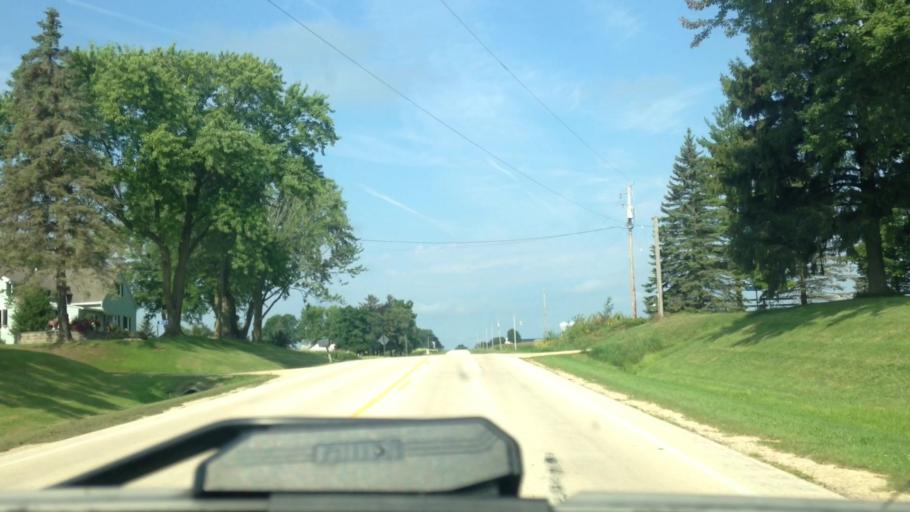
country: US
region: Wisconsin
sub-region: Dodge County
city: Theresa
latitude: 43.5366
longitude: -88.4817
